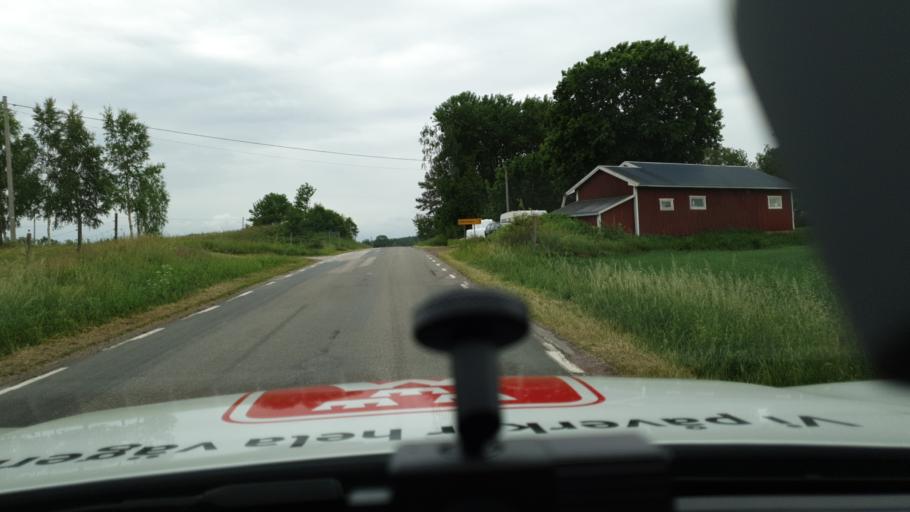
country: SE
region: Vaestra Goetaland
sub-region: Skovde Kommun
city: Stopen
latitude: 58.5005
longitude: 13.8729
